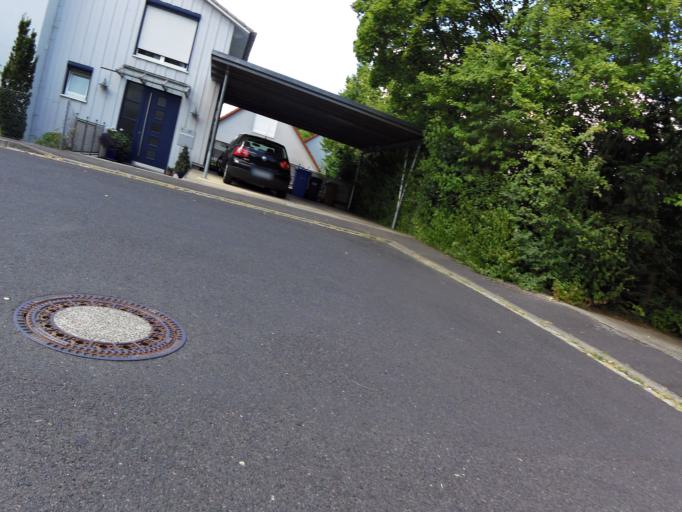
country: DE
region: Bavaria
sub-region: Regierungsbezirk Unterfranken
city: Hochberg
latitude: 49.7862
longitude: 9.8804
